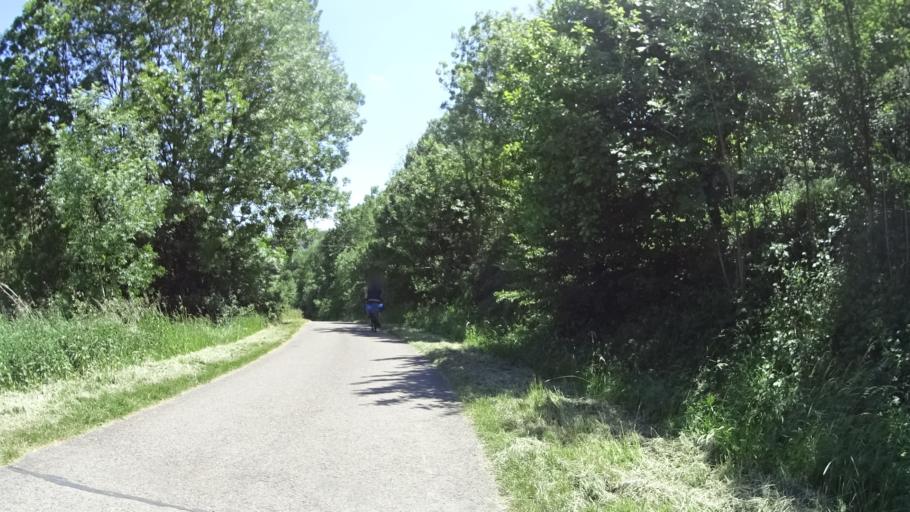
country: DE
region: Bavaria
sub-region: Regierungsbezirk Mittelfranken
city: Adelshofen
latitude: 49.4409
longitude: 10.1274
